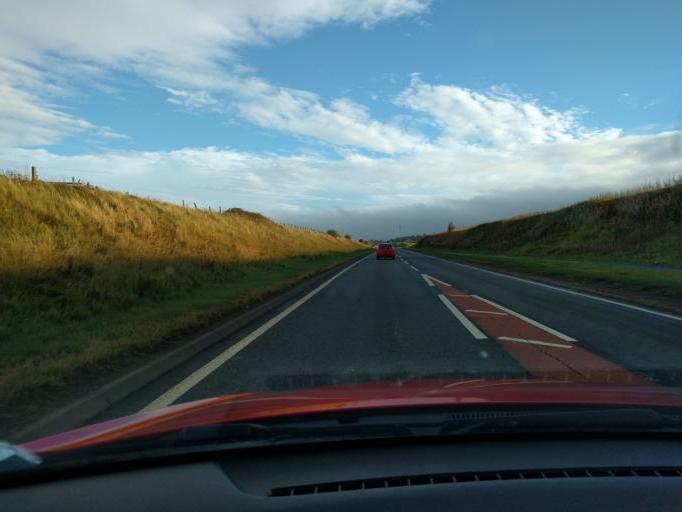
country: GB
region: Scotland
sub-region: East Lothian
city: Dunbar
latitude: 55.9544
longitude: -2.3931
